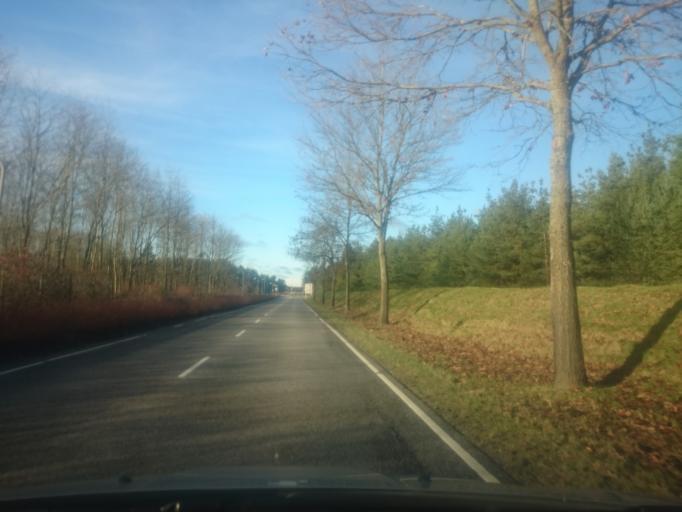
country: DK
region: South Denmark
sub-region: Billund Kommune
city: Billund
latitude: 55.7389
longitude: 9.1183
